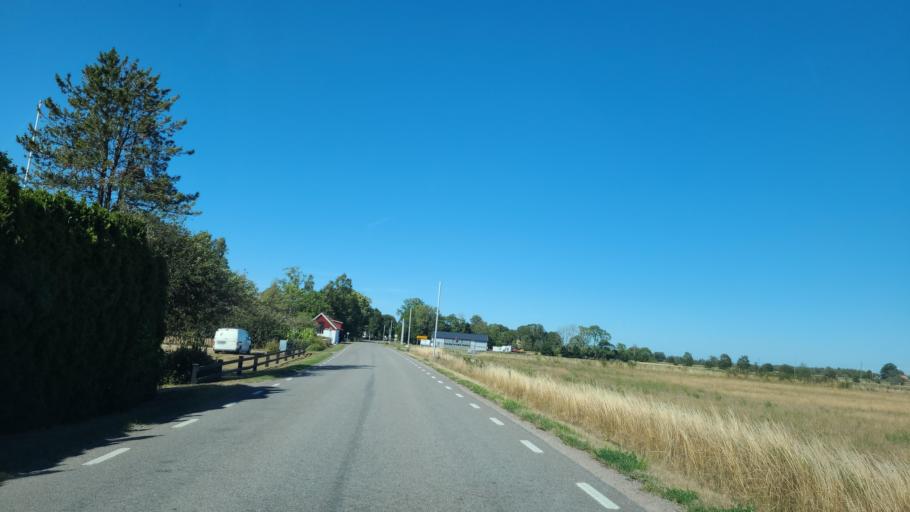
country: SE
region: Kalmar
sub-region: Borgholms Kommun
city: Borgholm
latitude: 56.9137
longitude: 16.8378
